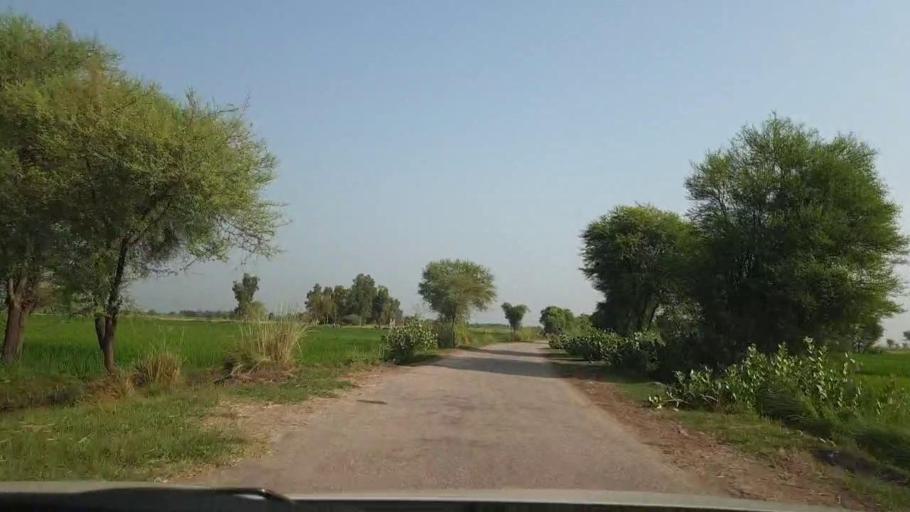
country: PK
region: Sindh
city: Goth Garelo
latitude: 27.4716
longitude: 68.1185
